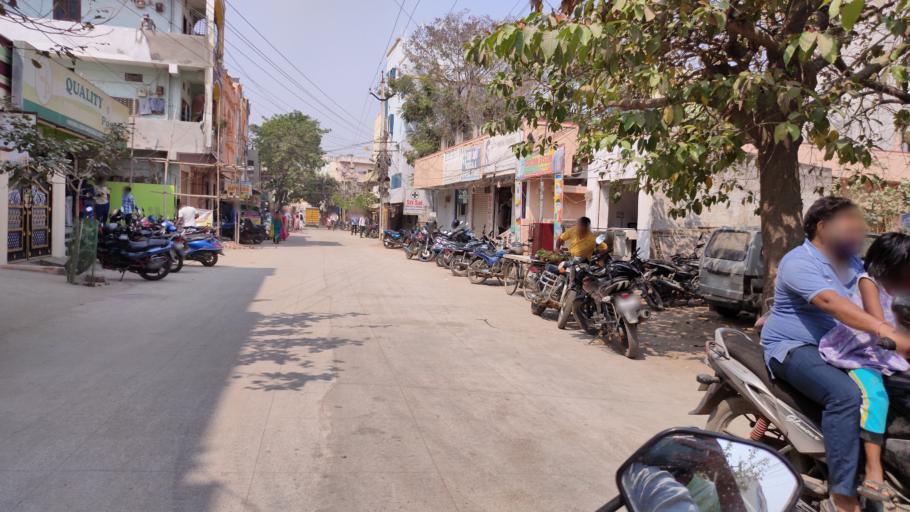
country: IN
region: Telangana
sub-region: Rangareddi
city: Quthbullapur
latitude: 17.4944
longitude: 78.4594
